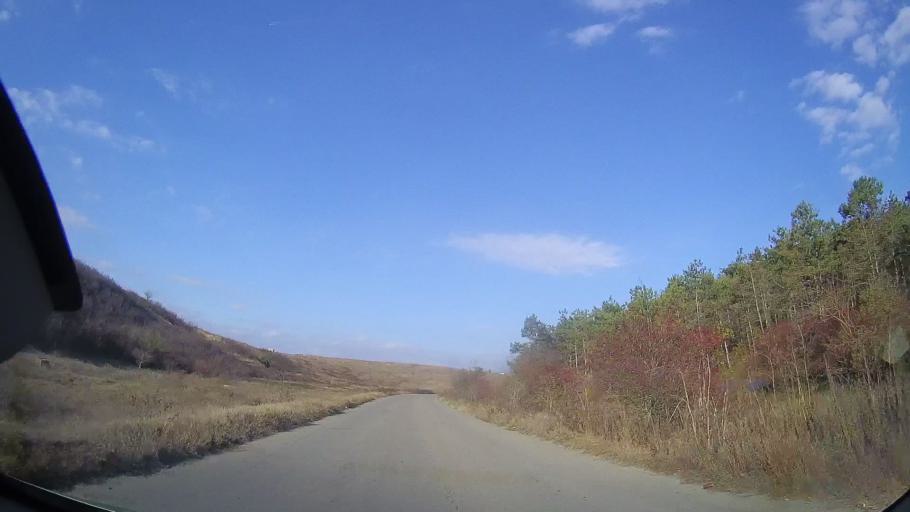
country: RO
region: Constanta
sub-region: Comuna Limanu
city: Limanu
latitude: 43.8171
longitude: 28.5177
